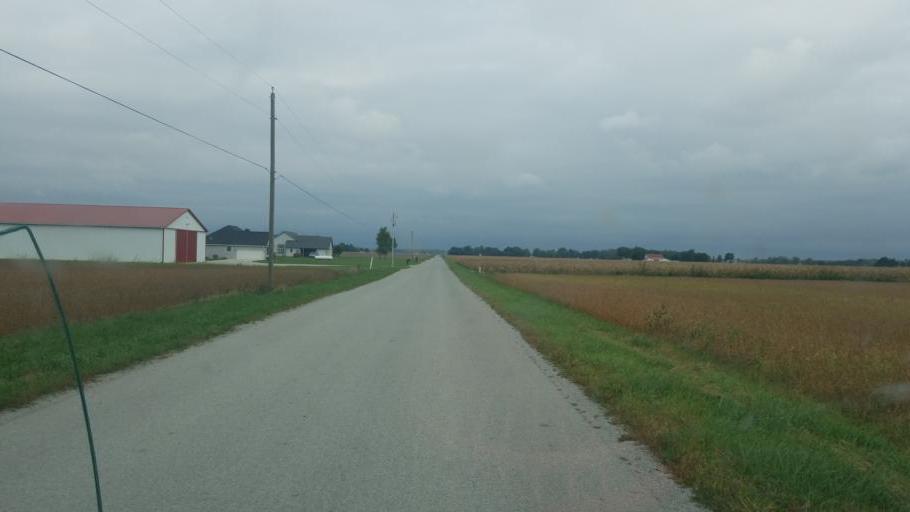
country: US
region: Ohio
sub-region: Wood County
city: Bowling Green
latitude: 41.3188
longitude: -83.6698
